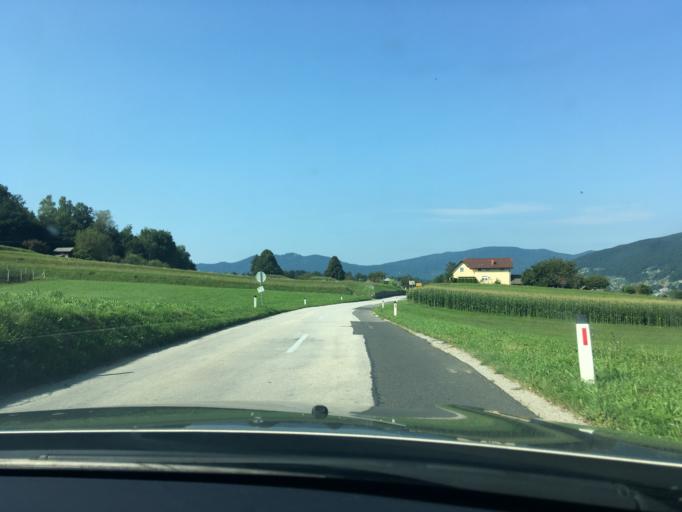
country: SI
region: Straza
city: Straza
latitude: 45.7865
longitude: 15.1054
